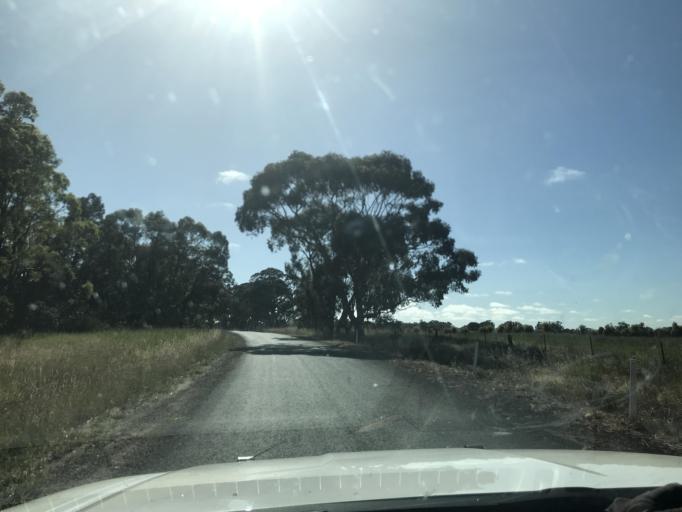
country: AU
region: Victoria
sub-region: Horsham
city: Horsham
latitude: -37.0406
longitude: 141.7353
